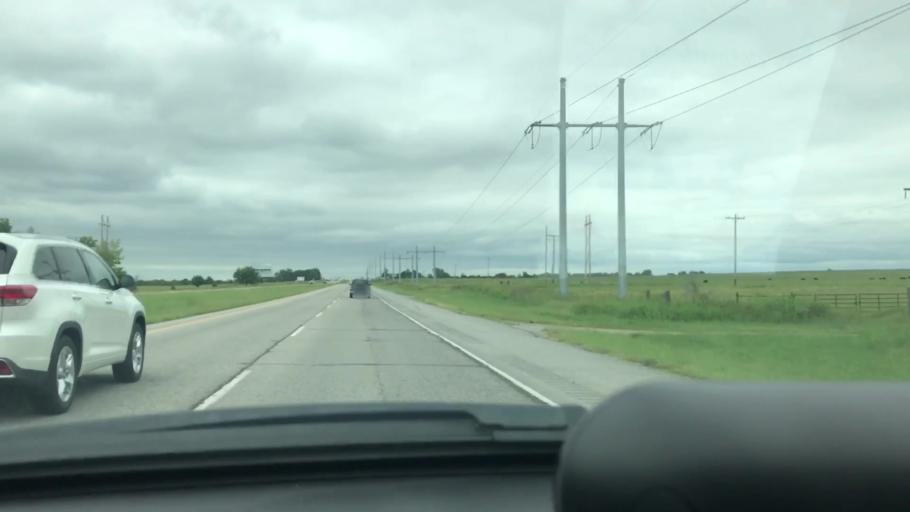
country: US
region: Oklahoma
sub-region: Wagoner County
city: Wagoner
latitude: 36.0062
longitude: -95.3683
